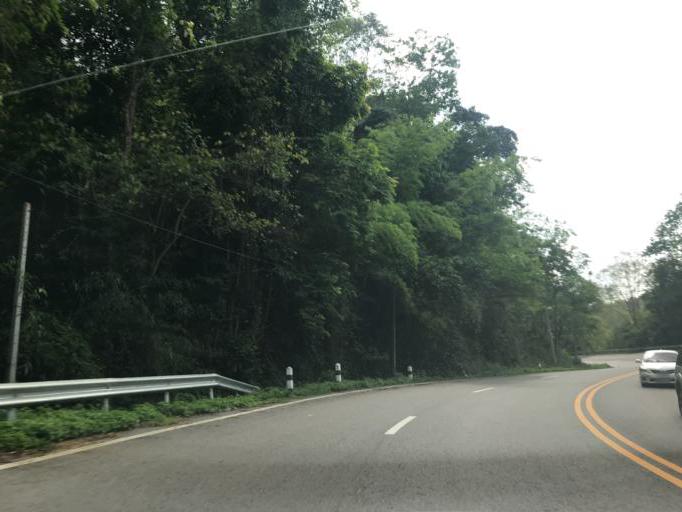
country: TH
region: Phayao
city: Phayao
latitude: 19.0682
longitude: 99.8105
